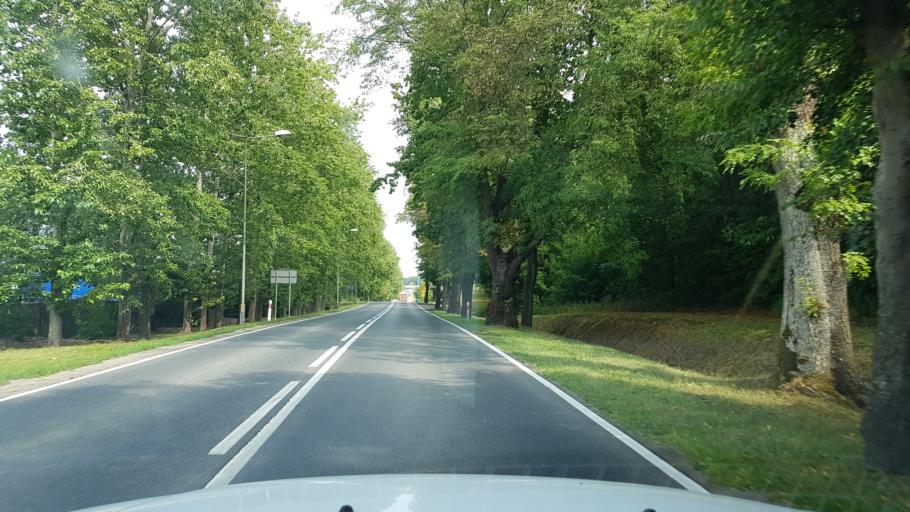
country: PL
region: West Pomeranian Voivodeship
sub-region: Powiat walecki
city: Walcz
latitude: 53.2812
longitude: 16.4952
